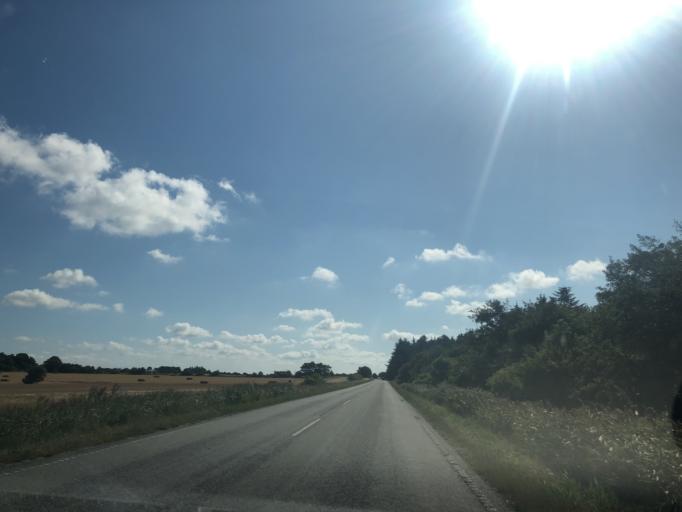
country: DK
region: North Denmark
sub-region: Morso Kommune
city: Nykobing Mors
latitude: 57.0100
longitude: 8.9606
